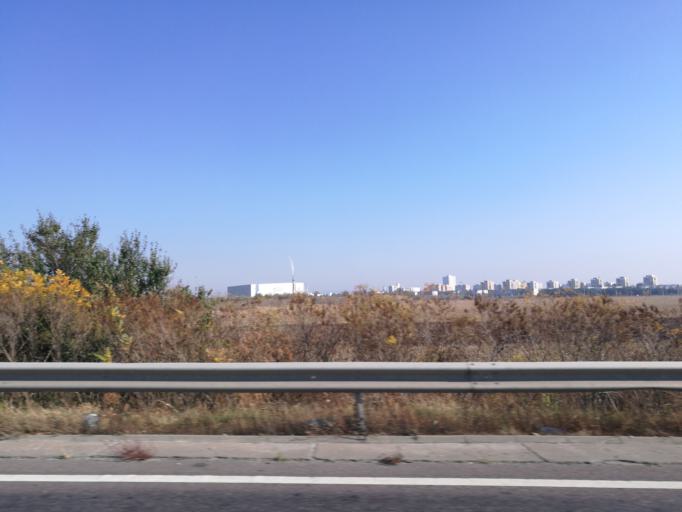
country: RO
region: Prahova
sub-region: Comuna Targsoru Vechi
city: Strejnicu
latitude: 44.9298
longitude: 25.9719
